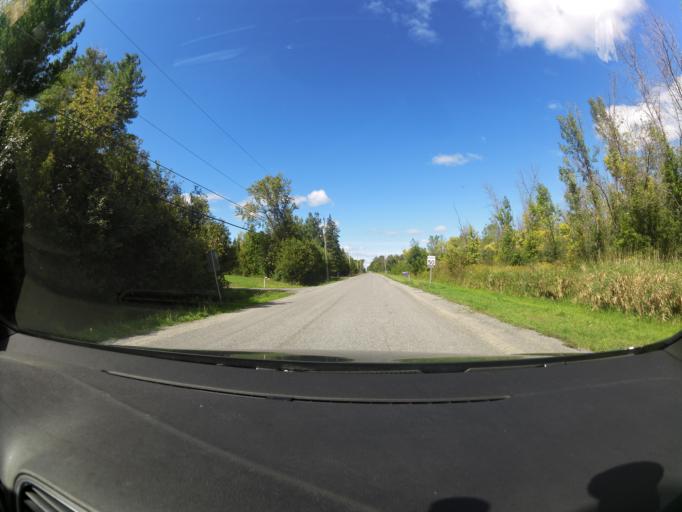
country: CA
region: Ontario
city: Carleton Place
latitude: 45.2361
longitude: -76.1542
